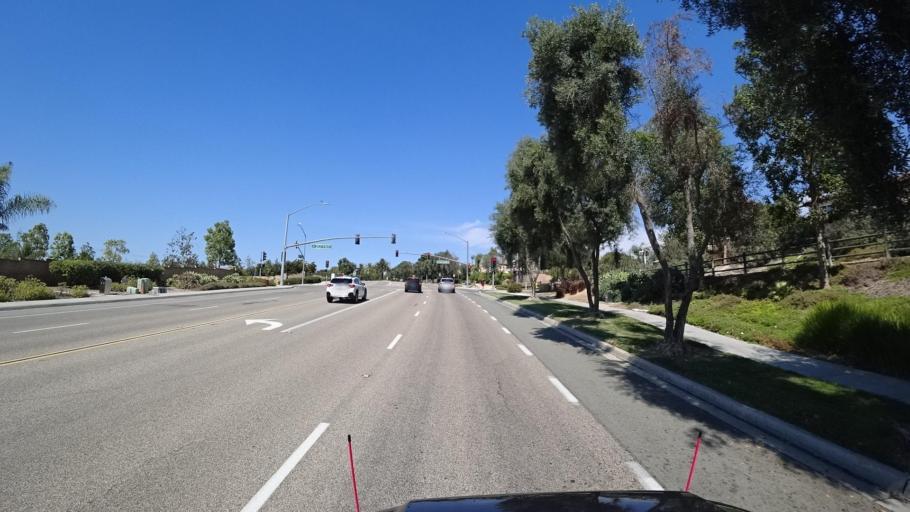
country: US
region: California
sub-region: San Diego County
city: La Presa
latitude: 32.6665
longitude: -116.9717
